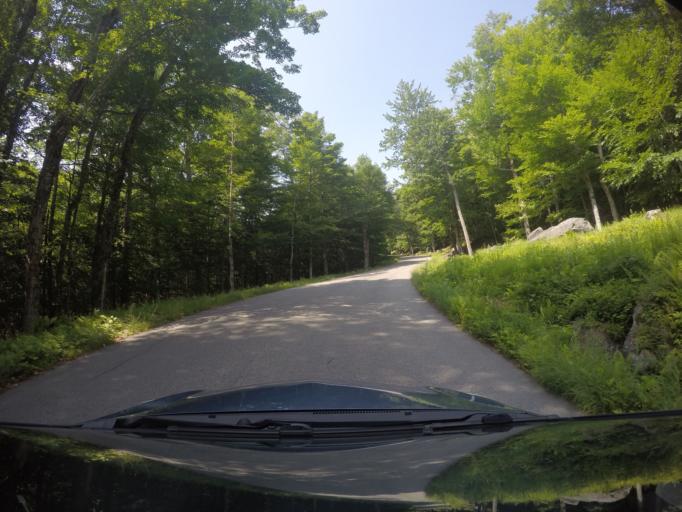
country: US
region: New Hampshire
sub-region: Coos County
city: Gorham
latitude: 44.2879
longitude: -71.2315
